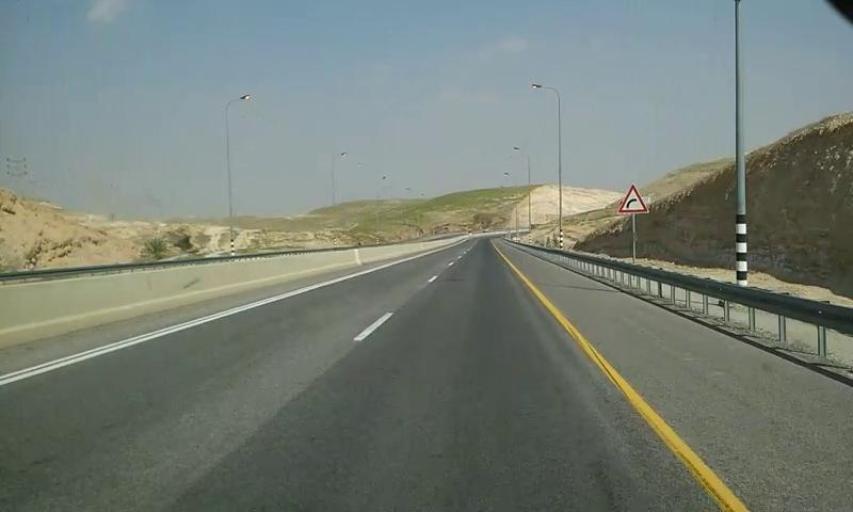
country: PS
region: West Bank
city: Jericho
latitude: 31.8210
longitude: 35.3826
